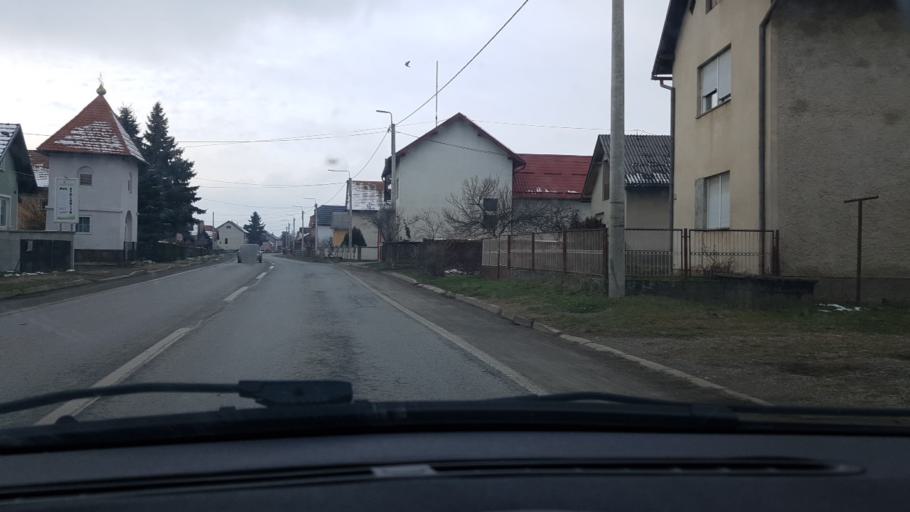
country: HR
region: Varazdinska
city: Nedeljanec
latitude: 46.2877
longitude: 16.2823
